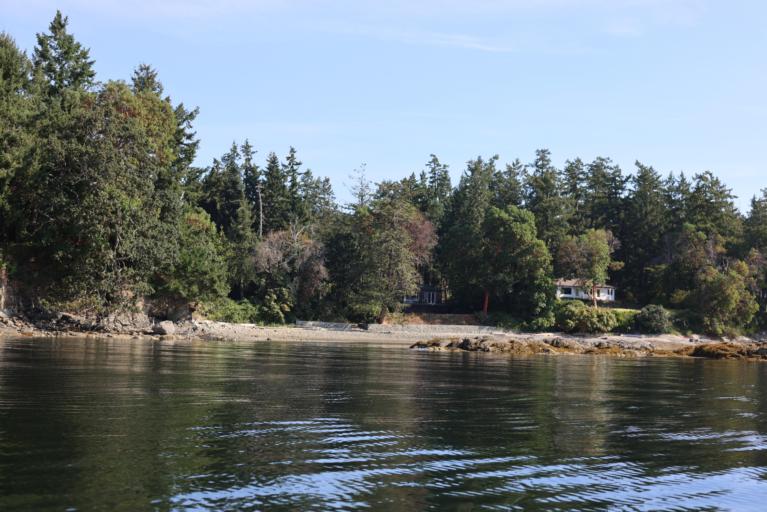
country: CA
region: British Columbia
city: North Saanich
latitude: 48.6676
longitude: -123.4774
